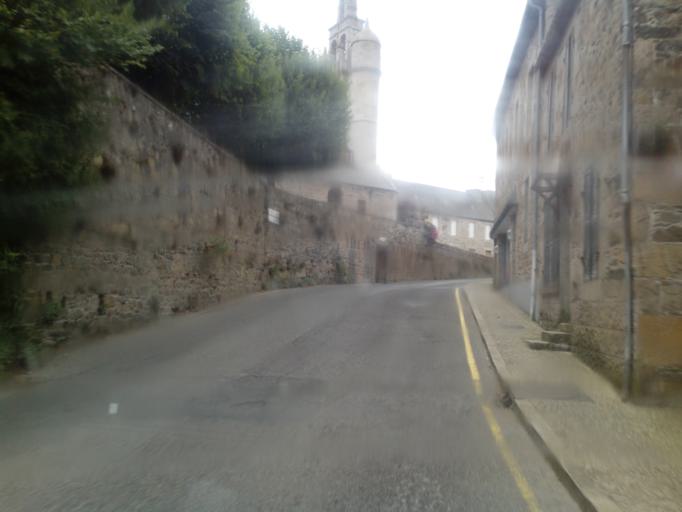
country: FR
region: Brittany
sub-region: Departement des Cotes-d'Armor
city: Lezardrieux
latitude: 48.7870
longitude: -3.1048
